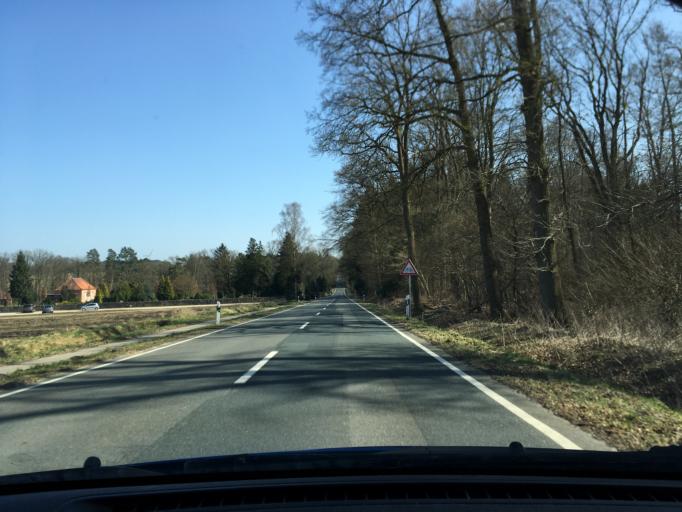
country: DE
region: Lower Saxony
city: Amelinghausen
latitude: 53.1198
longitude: 10.2203
